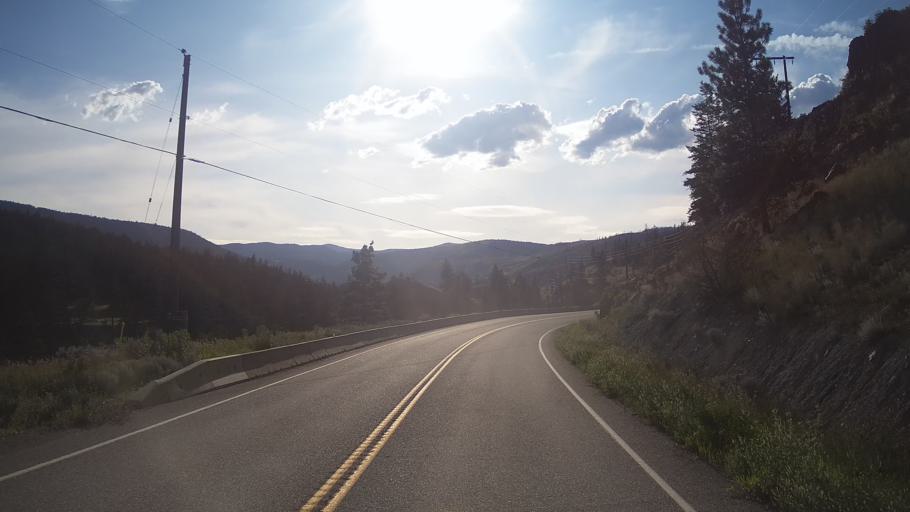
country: CA
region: British Columbia
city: Cache Creek
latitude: 50.8860
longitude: -121.4359
